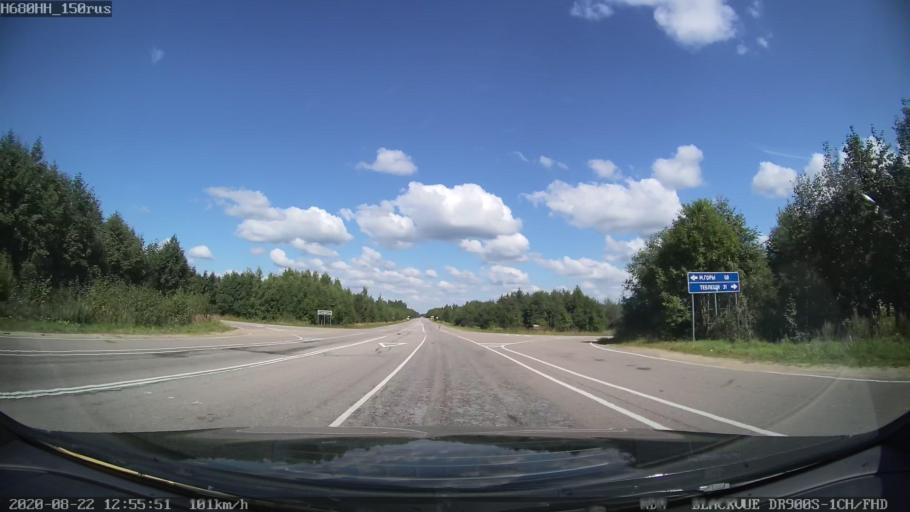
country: RU
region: Tverskaya
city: Rameshki
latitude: 57.5480
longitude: 36.3094
